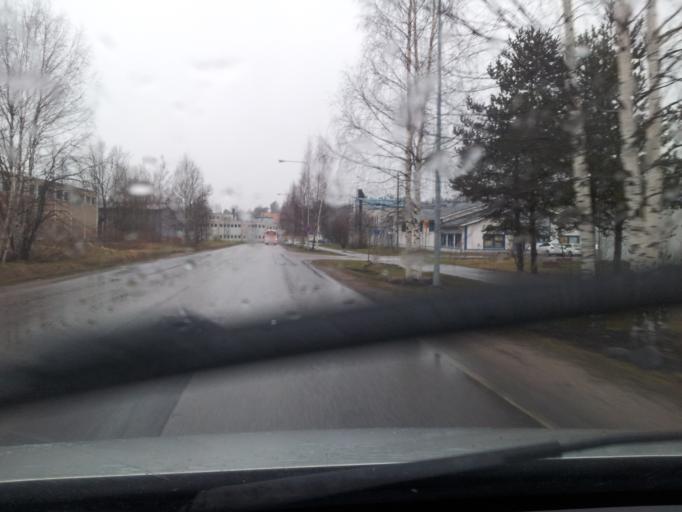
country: FI
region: Uusimaa
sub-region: Helsinki
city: Espoo
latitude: 60.1872
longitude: 24.6100
